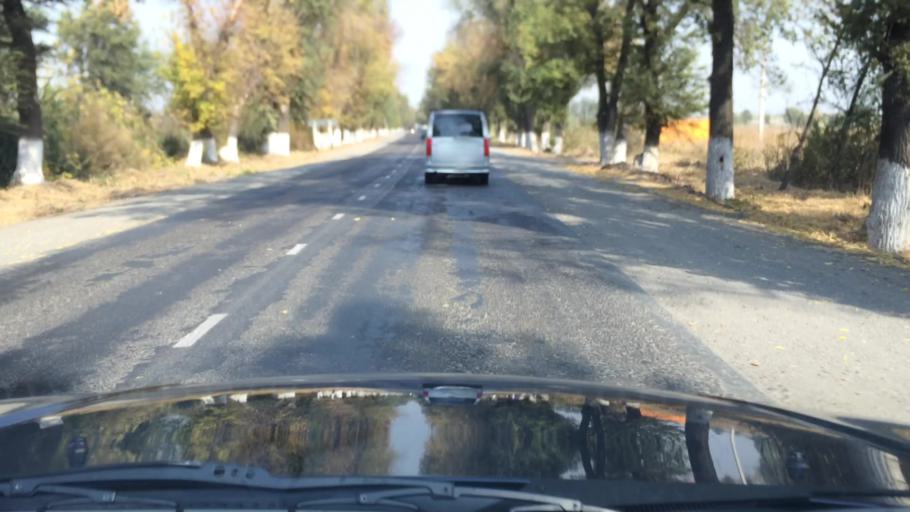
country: KG
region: Chuy
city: Lebedinovka
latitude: 42.9250
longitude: 74.6904
